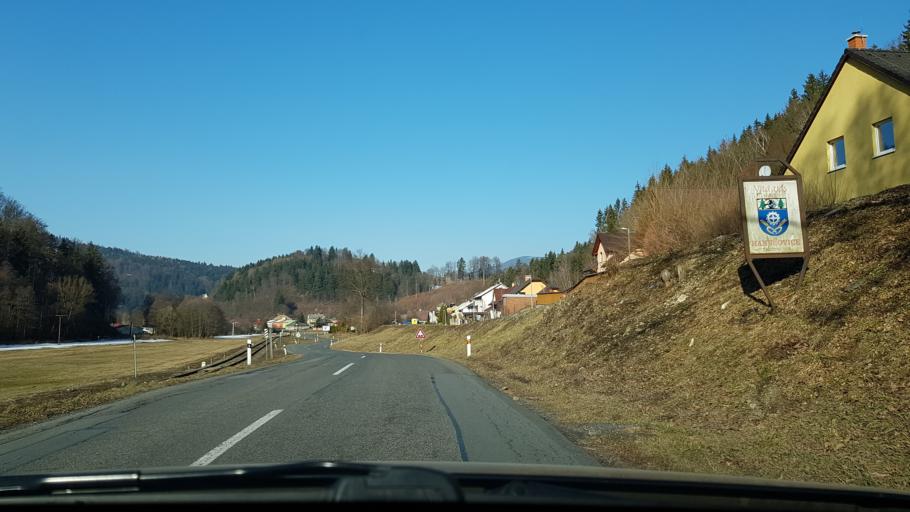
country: CZ
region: Olomoucky
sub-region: Okres Sumperk
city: Hanusovice
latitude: 50.0784
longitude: 16.9481
